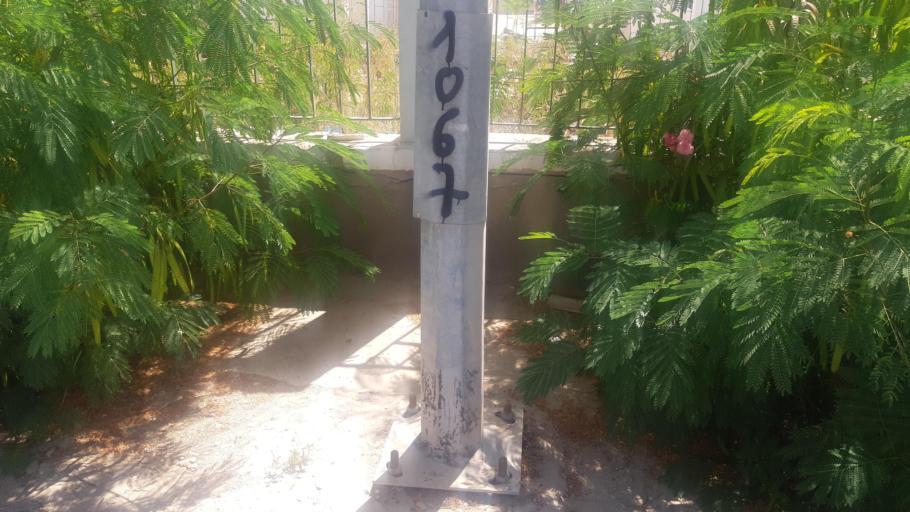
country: TN
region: Safaqis
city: Sfax
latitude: 34.7696
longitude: 10.7616
